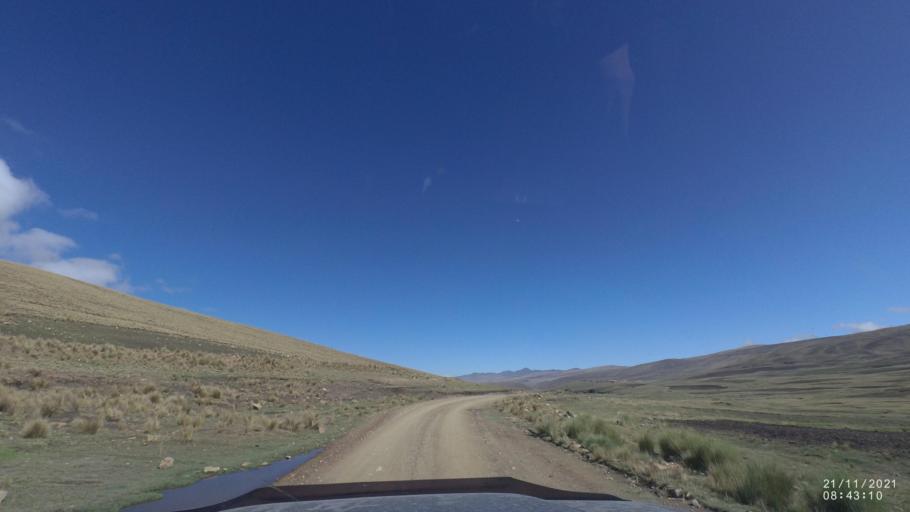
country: BO
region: Cochabamba
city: Cochabamba
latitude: -17.2625
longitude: -66.2239
